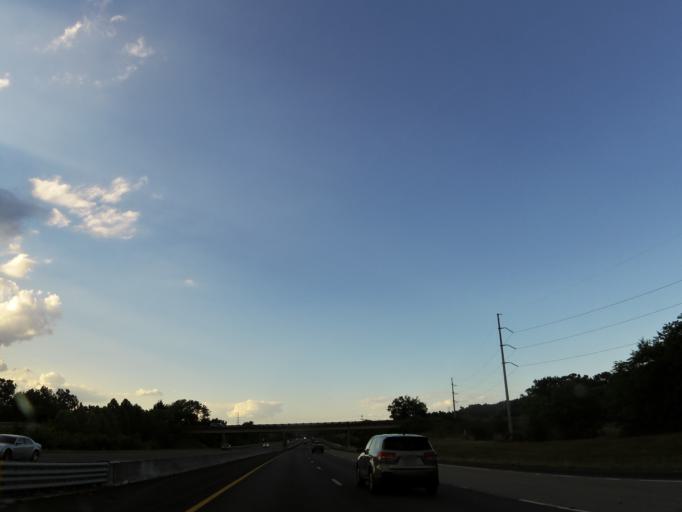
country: US
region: Tennessee
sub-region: Maury County
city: Spring Hill
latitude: 35.7498
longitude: -86.8706
